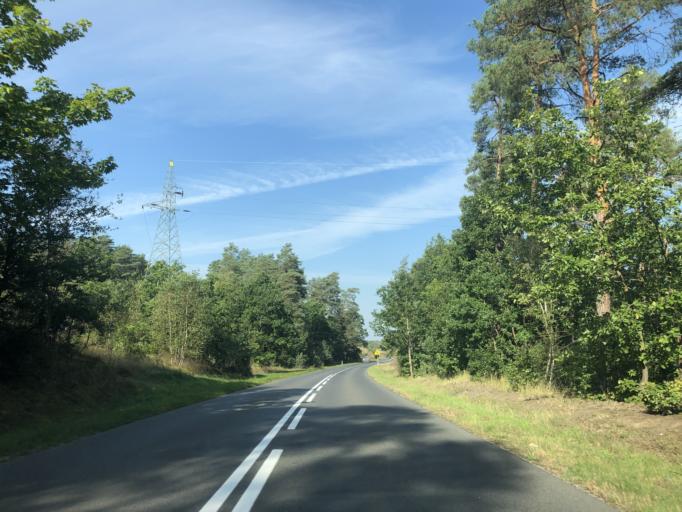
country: PL
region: Greater Poland Voivodeship
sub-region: Powiat pilski
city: Pila
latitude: 53.1287
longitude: 16.8065
